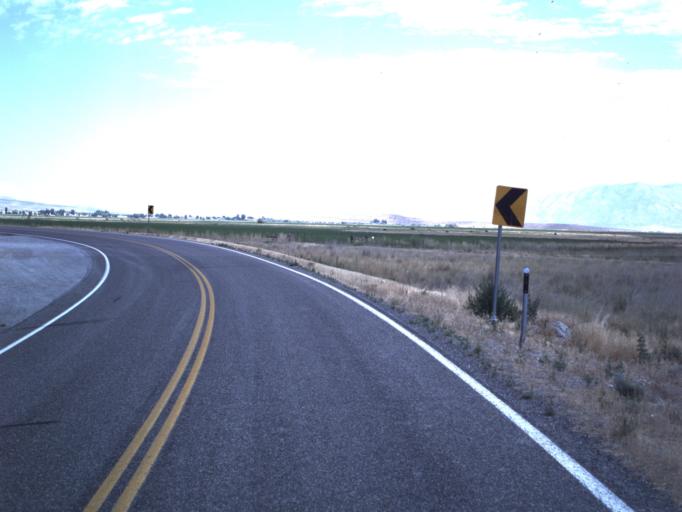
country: US
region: Utah
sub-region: Box Elder County
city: Tremonton
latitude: 41.6271
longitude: -112.3318
